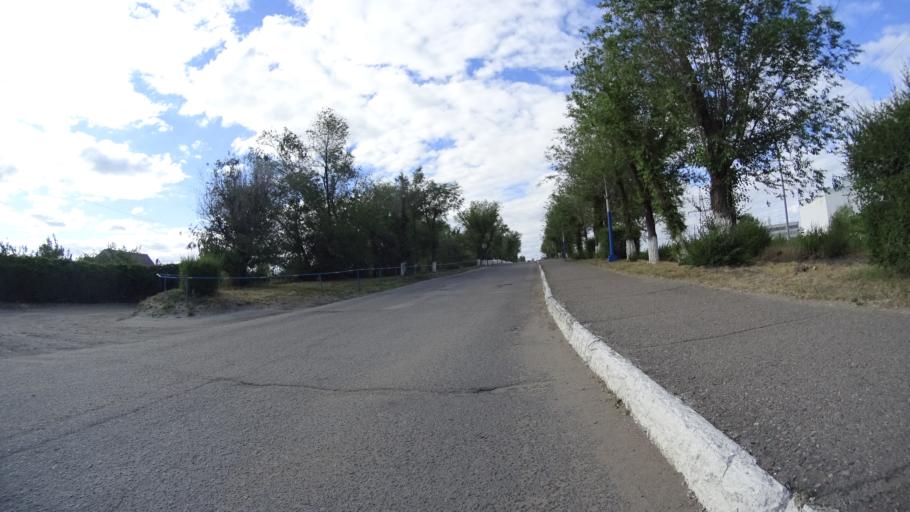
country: RU
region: Chelyabinsk
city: Troitsk
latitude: 54.0379
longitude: 61.6399
